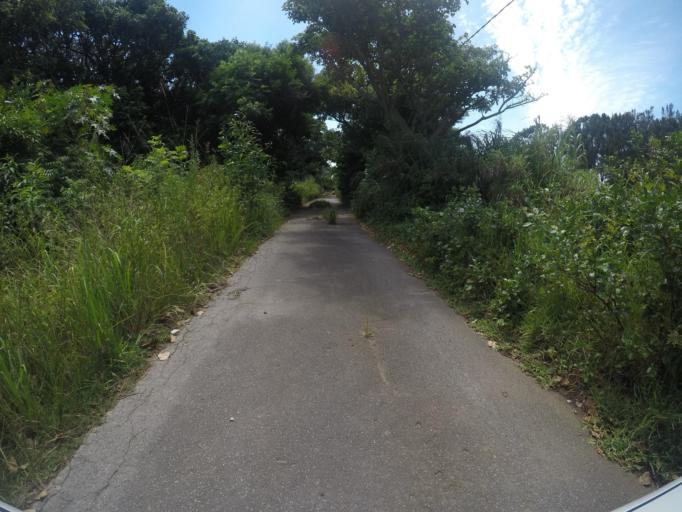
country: ZA
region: Eastern Cape
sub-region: Buffalo City Metropolitan Municipality
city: East London
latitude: -32.9526
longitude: 28.0018
